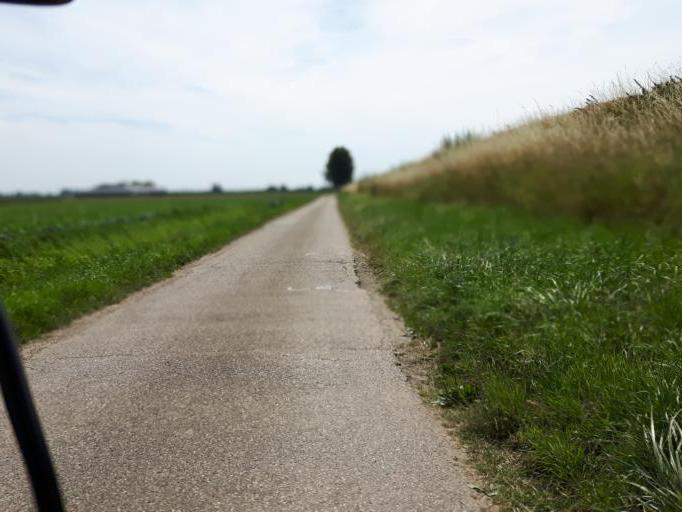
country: NL
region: North Brabant
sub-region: Gemeente Steenbergen
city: Nieuw-Vossemeer
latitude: 51.6221
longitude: 4.2238
